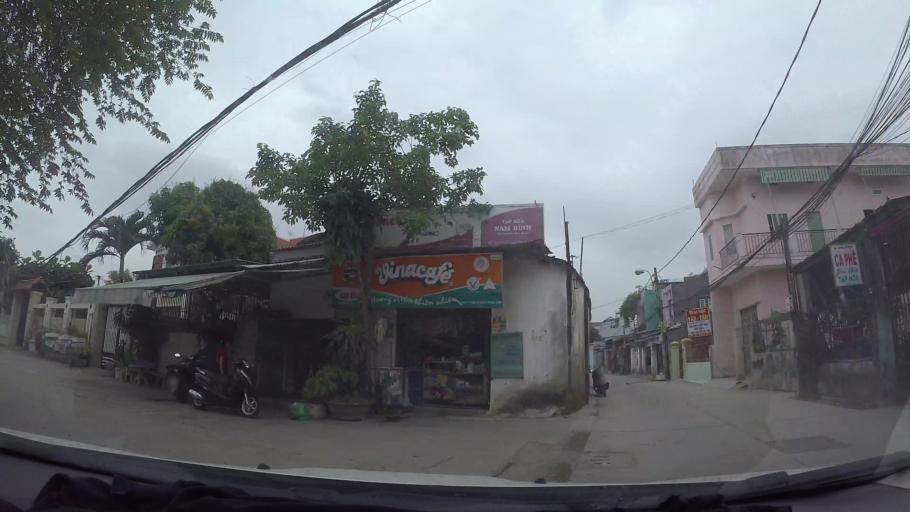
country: VN
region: Da Nang
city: Lien Chieu
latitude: 16.0874
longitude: 108.1434
